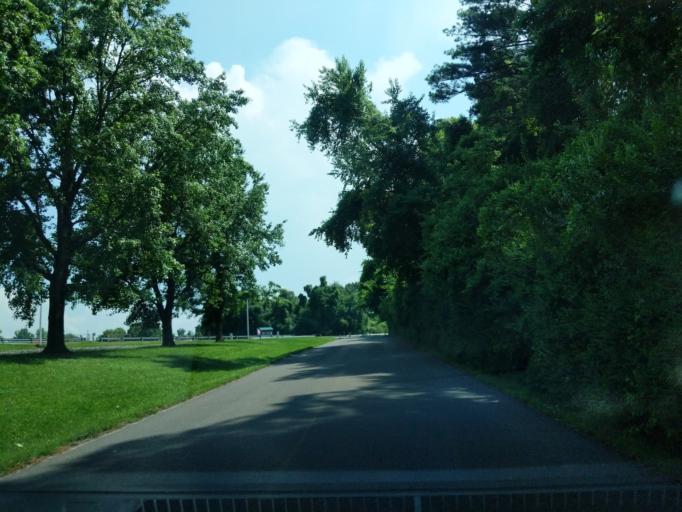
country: US
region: Tennessee
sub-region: Sumner County
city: Hendersonville
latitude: 36.2915
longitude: -86.6621
